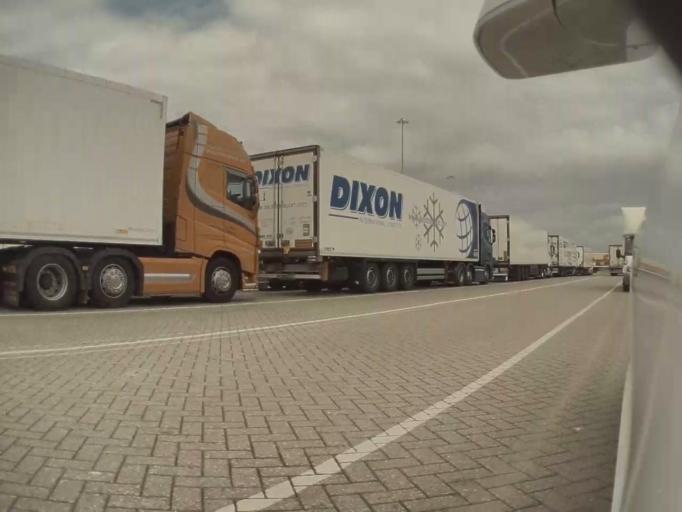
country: GB
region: Wales
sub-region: Anglesey
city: Holyhead
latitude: 53.3160
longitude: -4.6220
